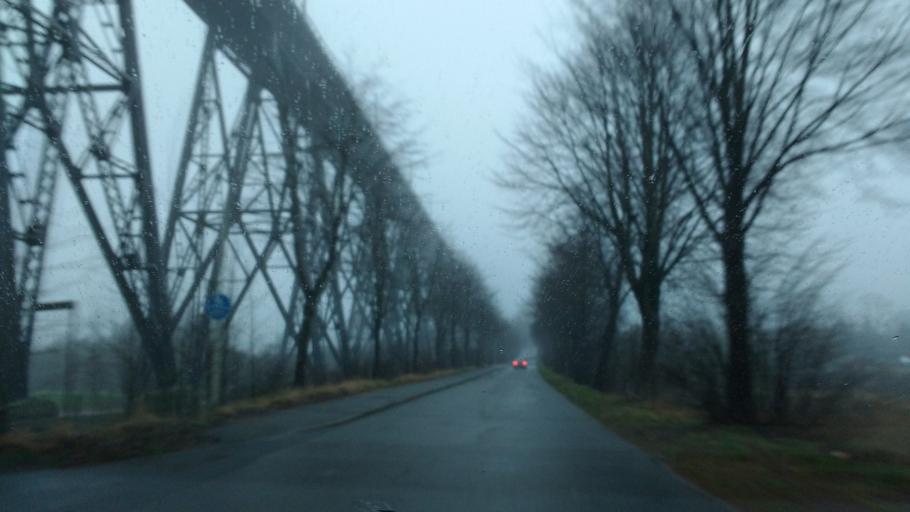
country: DE
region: Schleswig-Holstein
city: Osterronfeld
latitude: 54.2894
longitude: 9.6852
